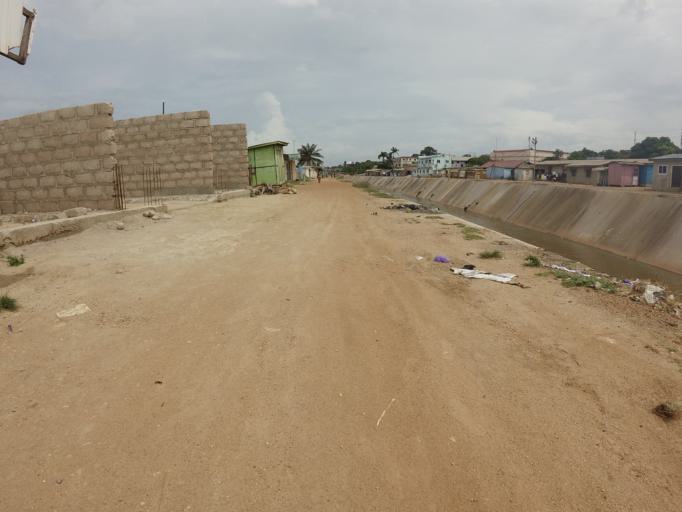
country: GH
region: Greater Accra
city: Accra
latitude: 5.5987
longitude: -0.2209
